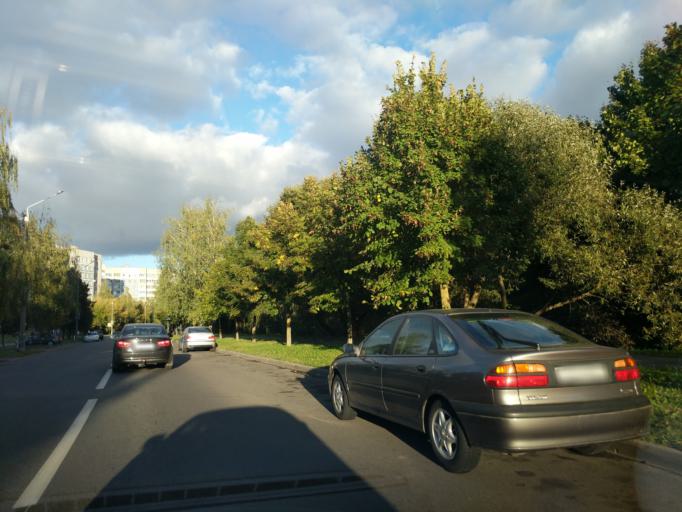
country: BY
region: Minsk
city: Malinovka
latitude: 53.8557
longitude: 27.4634
